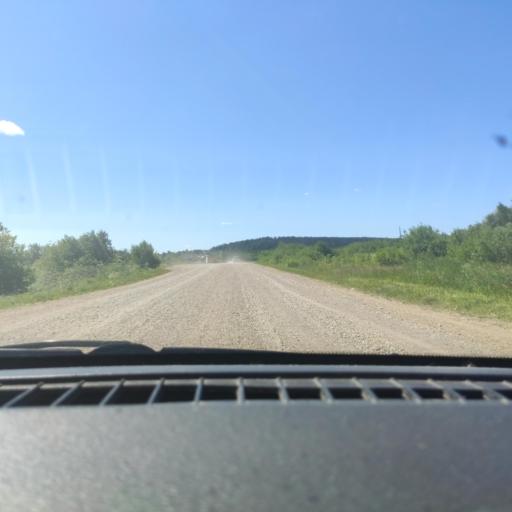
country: RU
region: Perm
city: Verkhnechusovskiye Gorodki
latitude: 58.1927
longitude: 57.1312
